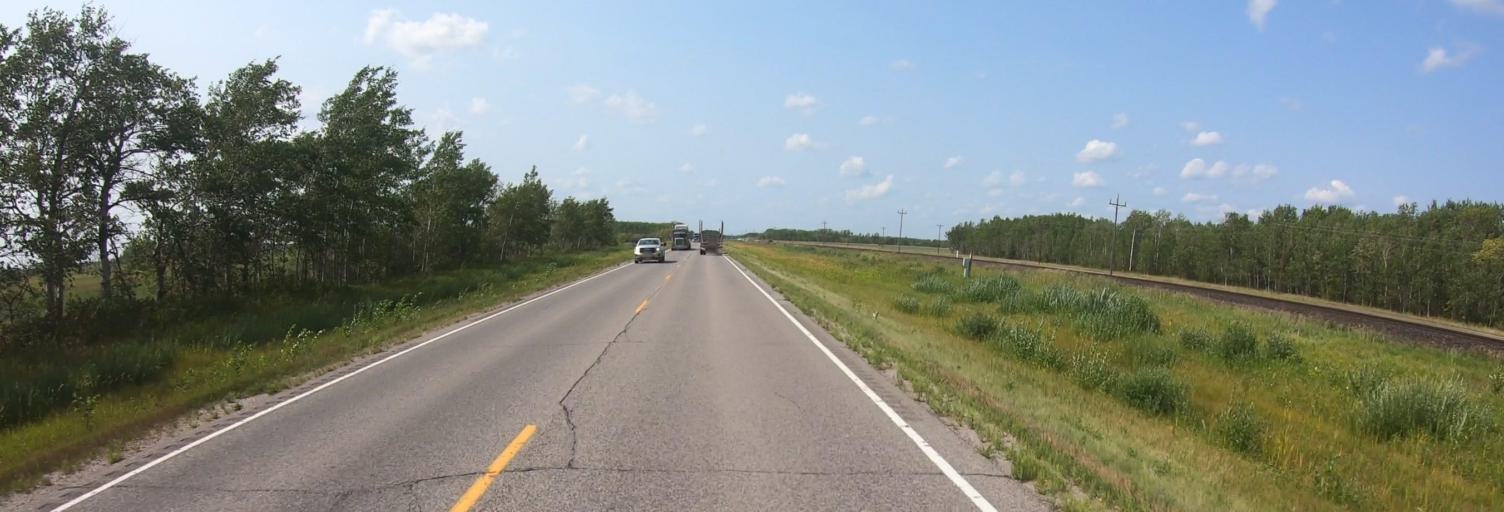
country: US
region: Minnesota
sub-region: Roseau County
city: Warroad
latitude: 48.8662
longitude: -95.2535
